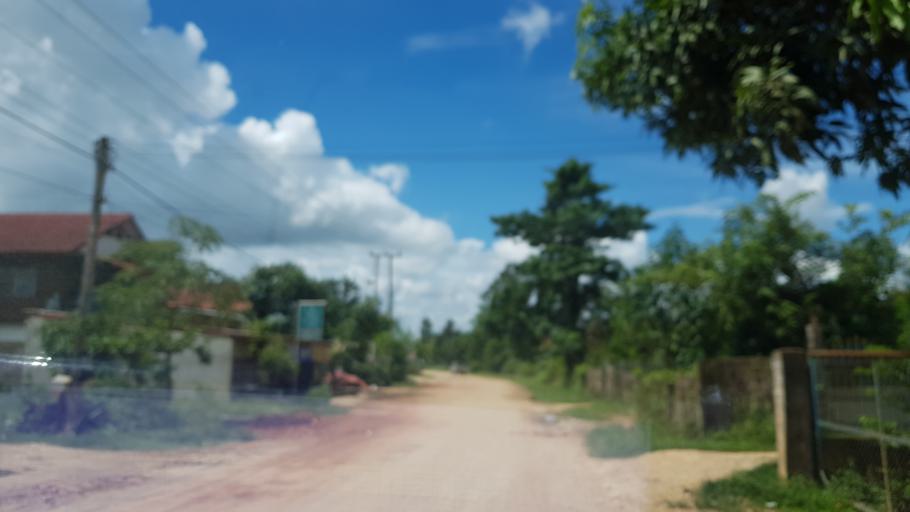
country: LA
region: Vientiane
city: Vientiane
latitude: 18.2169
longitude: 102.5160
